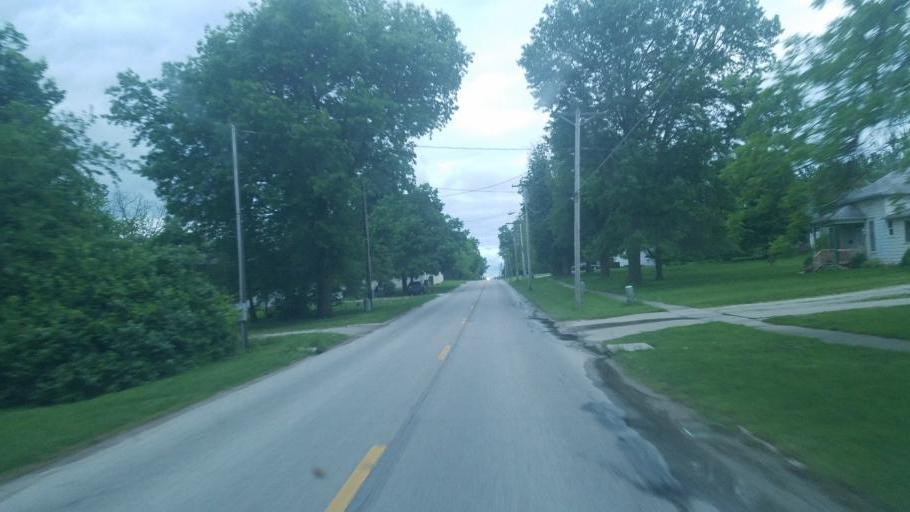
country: US
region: Iowa
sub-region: Decatur County
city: Lamoni
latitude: 40.6194
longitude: -93.9390
